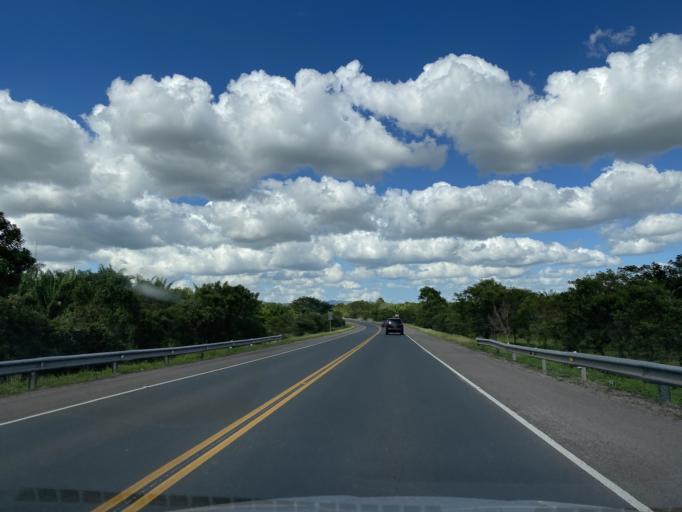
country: DO
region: Monte Plata
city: Monte Plata
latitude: 18.7284
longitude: -69.7609
